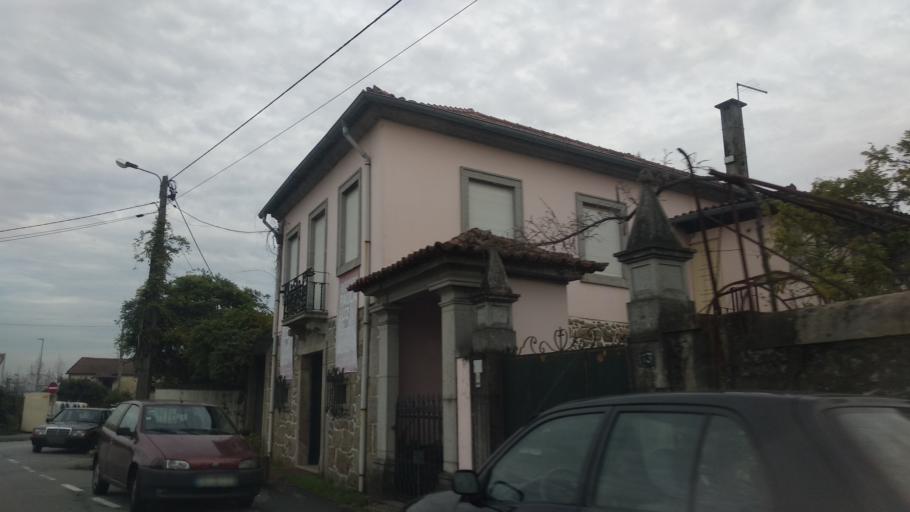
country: PT
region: Braga
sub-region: Braga
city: Braga
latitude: 41.5301
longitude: -8.4413
